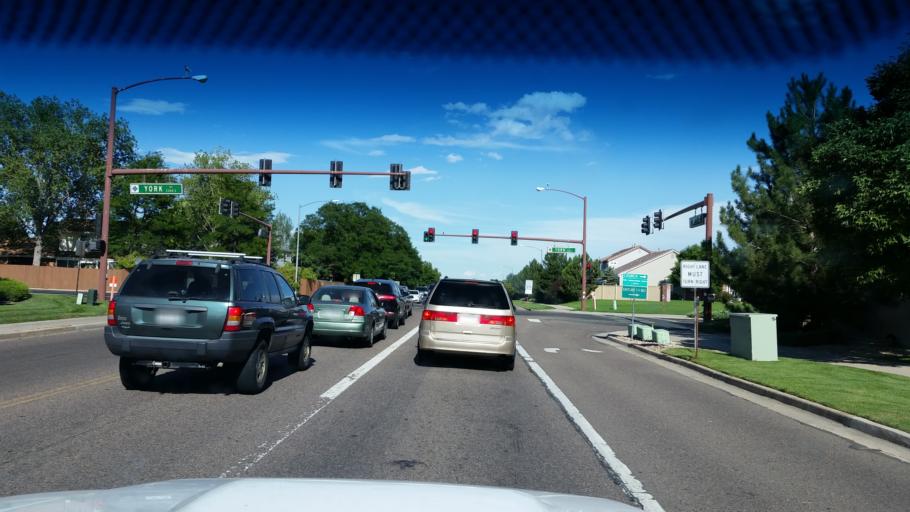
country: US
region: Colorado
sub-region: Adams County
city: Northglenn
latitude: 39.9284
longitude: -104.9597
